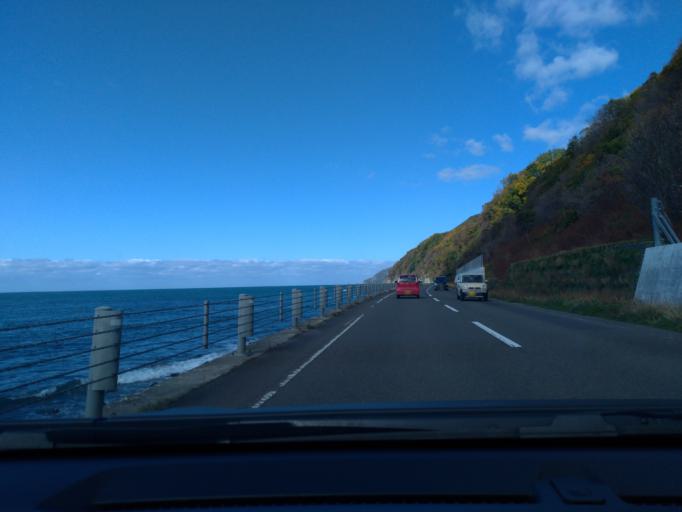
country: JP
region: Hokkaido
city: Ishikari
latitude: 43.4320
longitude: 141.4200
